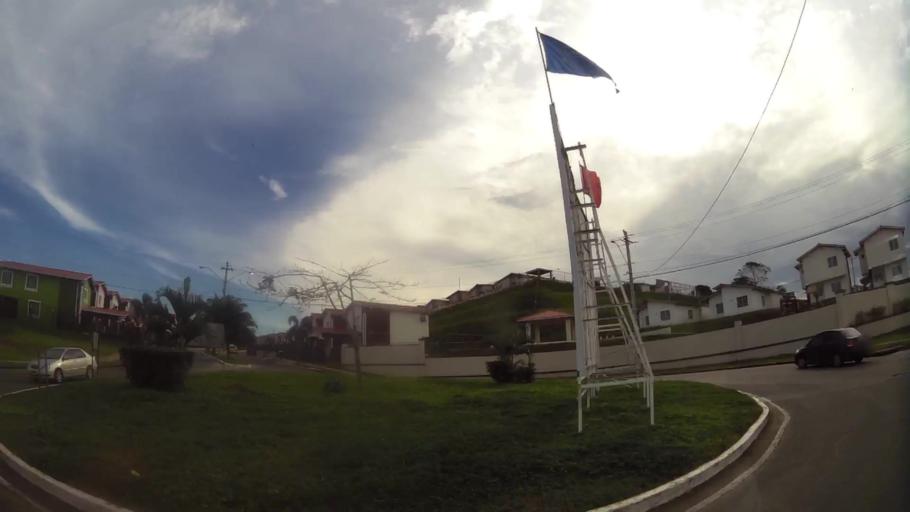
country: PA
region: Panama
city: La Chorrera
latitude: 8.8795
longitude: -79.7662
